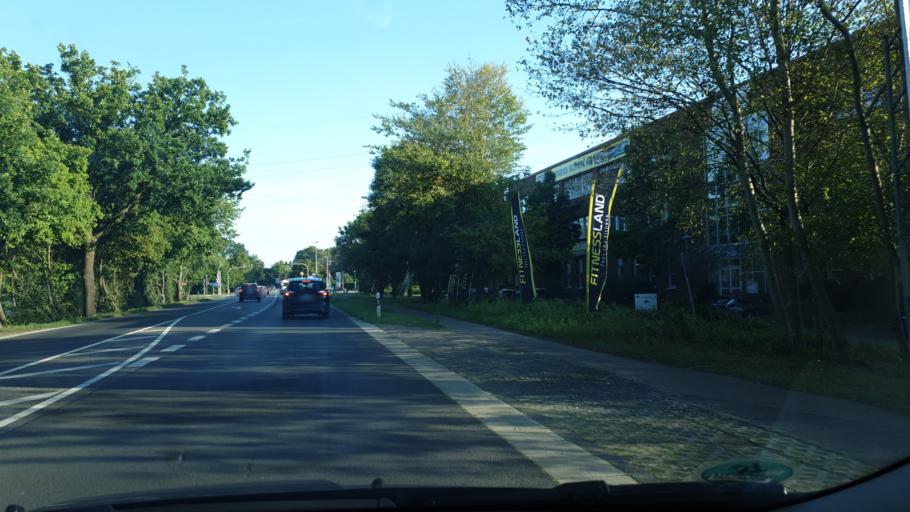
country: DE
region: North Rhine-Westphalia
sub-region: Regierungsbezirk Koln
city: Gremberghoven
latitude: 50.9097
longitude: 7.0580
